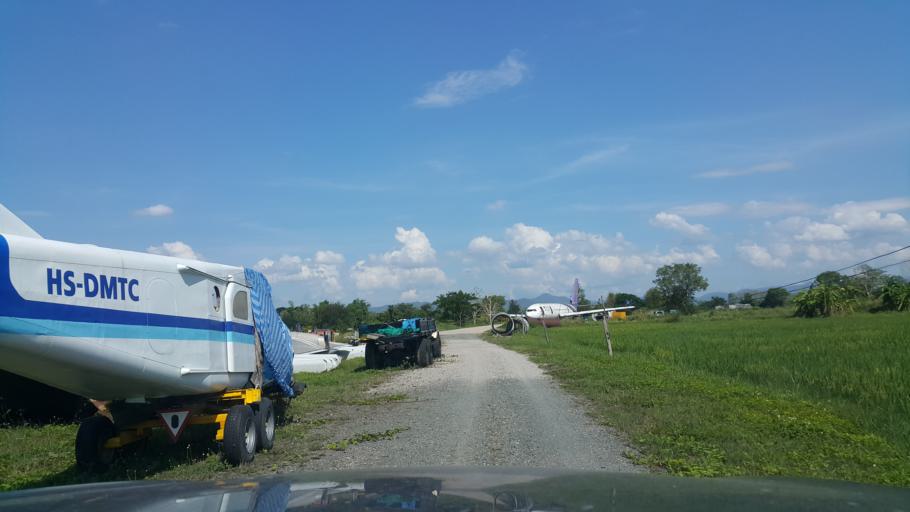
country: TH
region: Chiang Mai
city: San Kamphaeng
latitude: 18.8051
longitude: 99.1177
